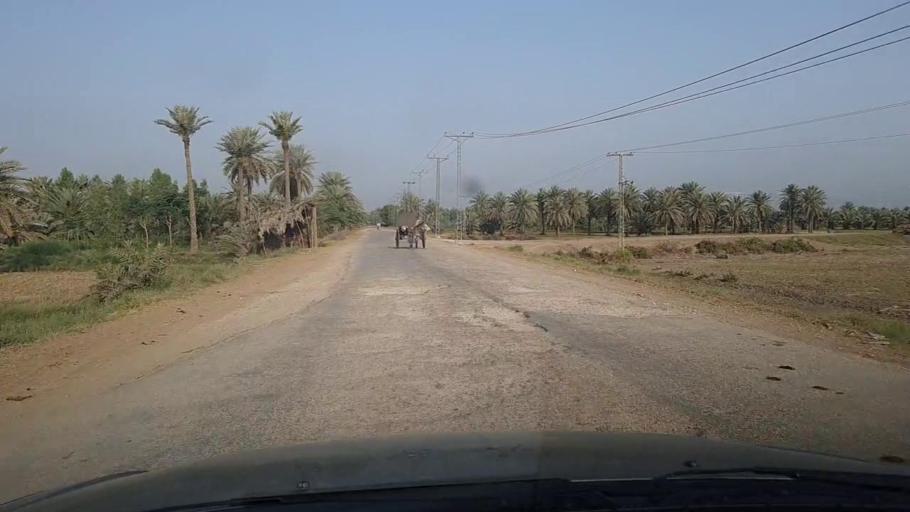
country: PK
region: Sindh
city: Pir jo Goth
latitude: 27.5709
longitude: 68.6262
